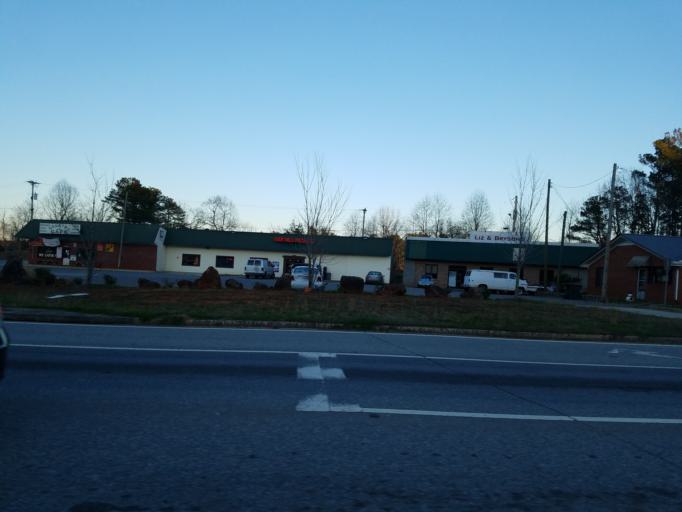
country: US
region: Georgia
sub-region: Dawson County
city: Dawsonville
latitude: 34.3403
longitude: -84.0228
